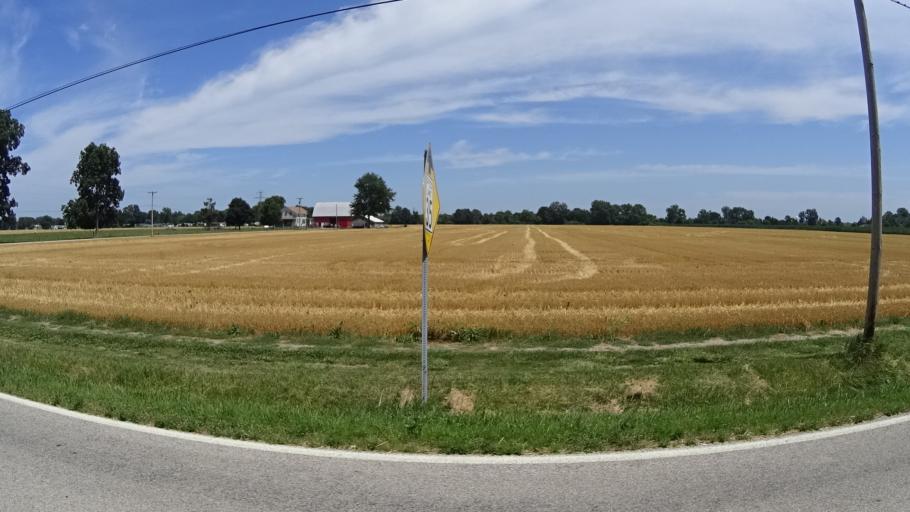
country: US
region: Ohio
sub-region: Erie County
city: Sandusky
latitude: 41.4326
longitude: -82.7724
